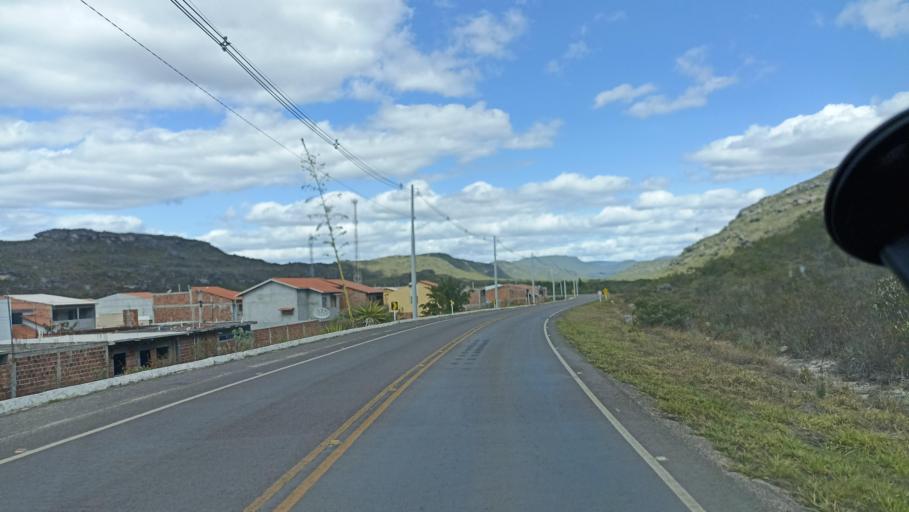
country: BR
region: Bahia
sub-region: Andarai
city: Vera Cruz
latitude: -13.0110
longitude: -41.3744
